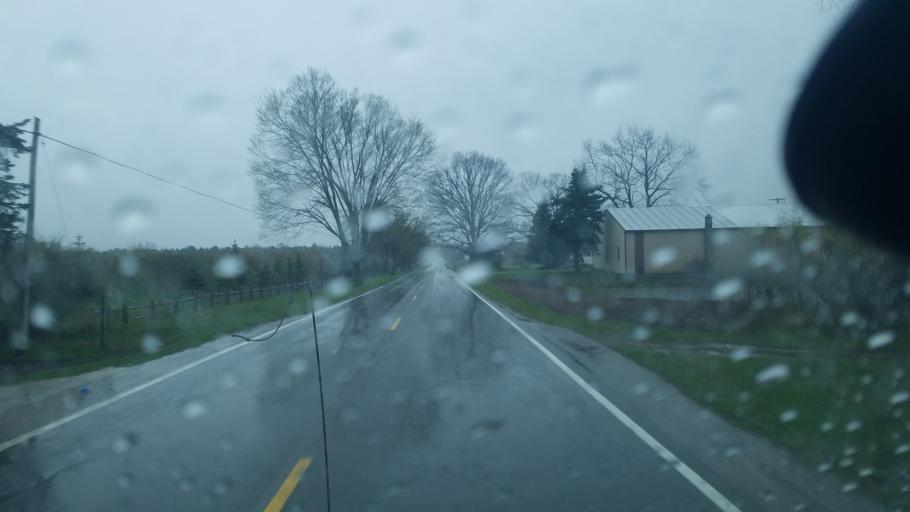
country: US
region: Michigan
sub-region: Montcalm County
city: Lakeview
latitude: 43.4644
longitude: -85.2737
